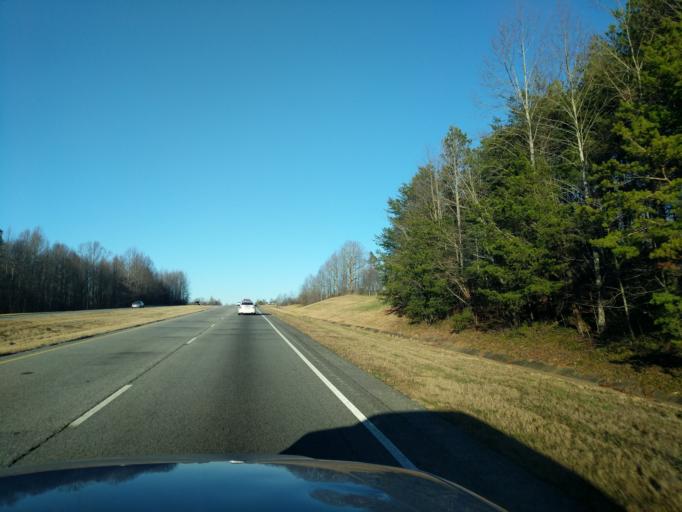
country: US
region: Georgia
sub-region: Habersham County
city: Clarkesville
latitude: 34.5828
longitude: -83.4556
